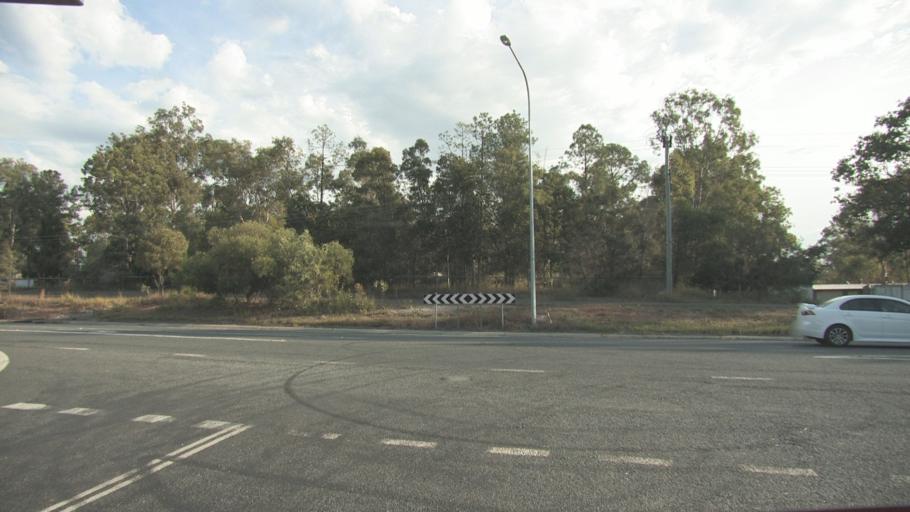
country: AU
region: Queensland
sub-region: Logan
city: Cedar Vale
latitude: -27.8446
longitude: 153.1191
